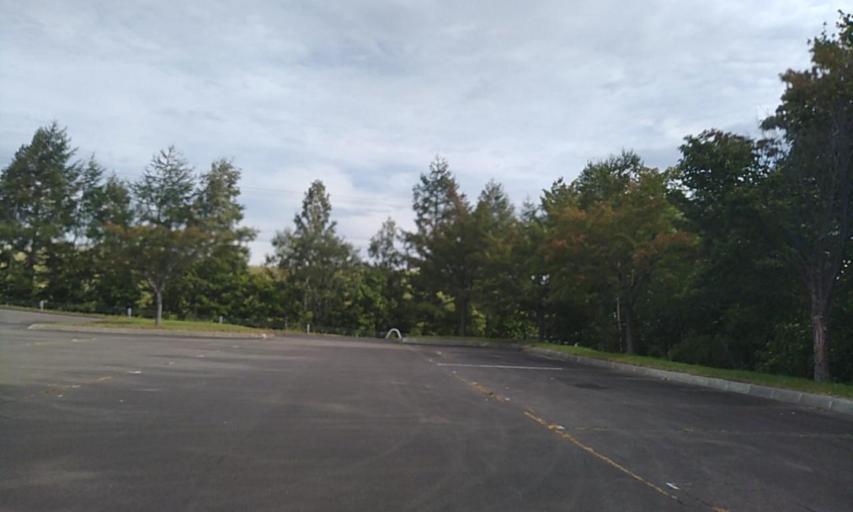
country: JP
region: Hokkaido
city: Abashiri
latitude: 43.7961
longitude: 144.5745
